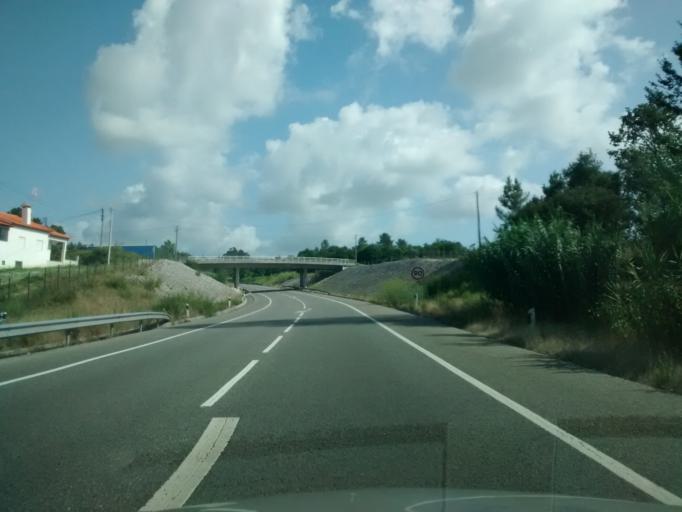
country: PT
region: Aveiro
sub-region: Anadia
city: Sangalhos
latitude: 40.4893
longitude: -8.4818
